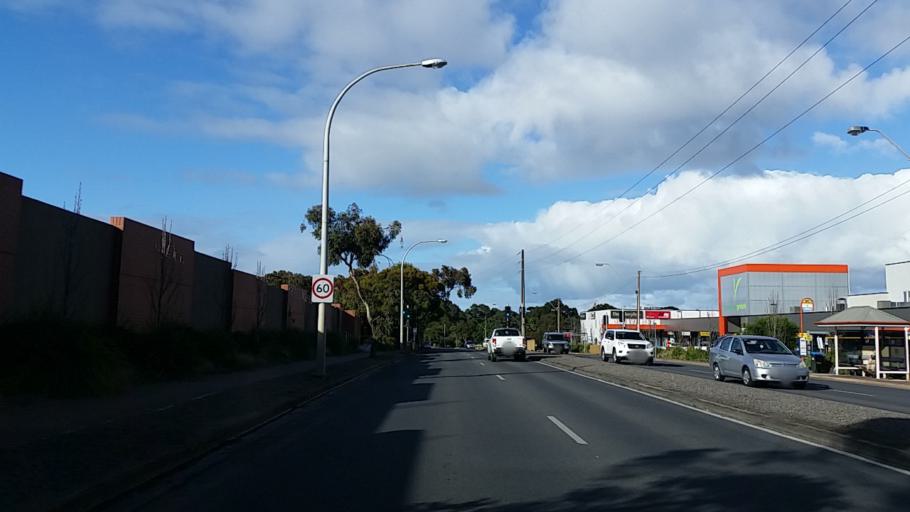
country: AU
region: South Australia
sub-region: Mitcham
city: Clapham
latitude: -35.0012
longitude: 138.5913
